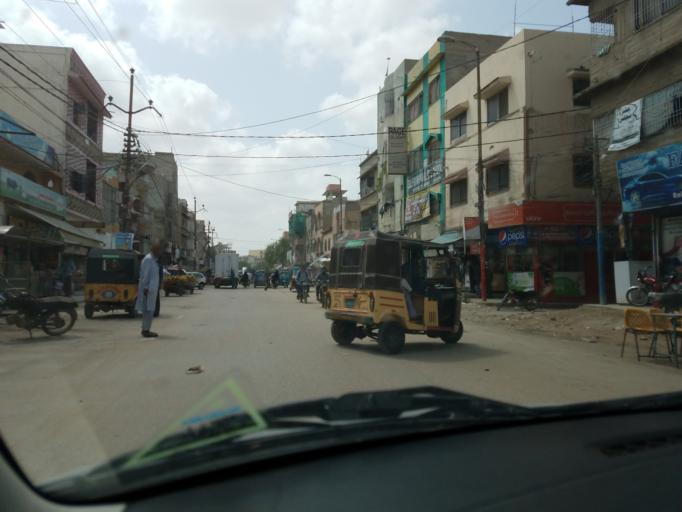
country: PK
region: Sindh
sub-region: Karachi District
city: Karachi
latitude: 24.9481
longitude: 67.0794
